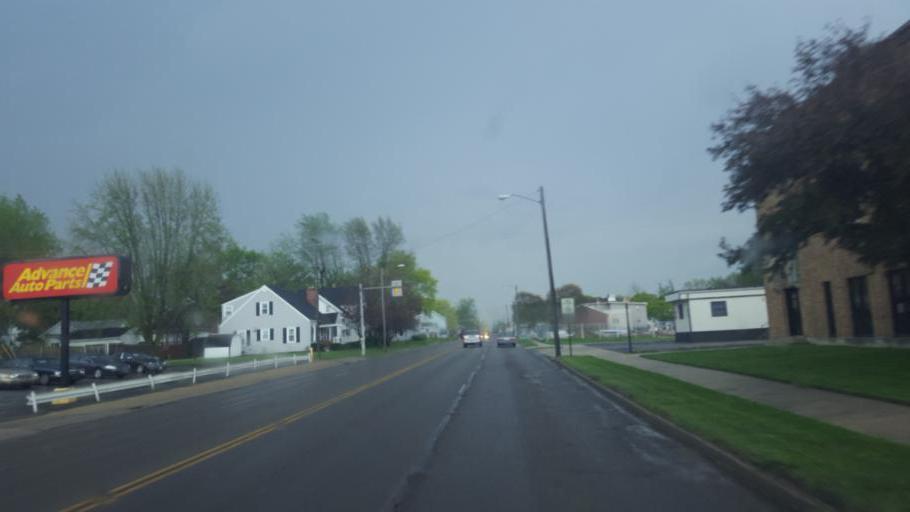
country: US
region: Ohio
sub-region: Seneca County
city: Fostoria
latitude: 41.1629
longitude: -83.4212
